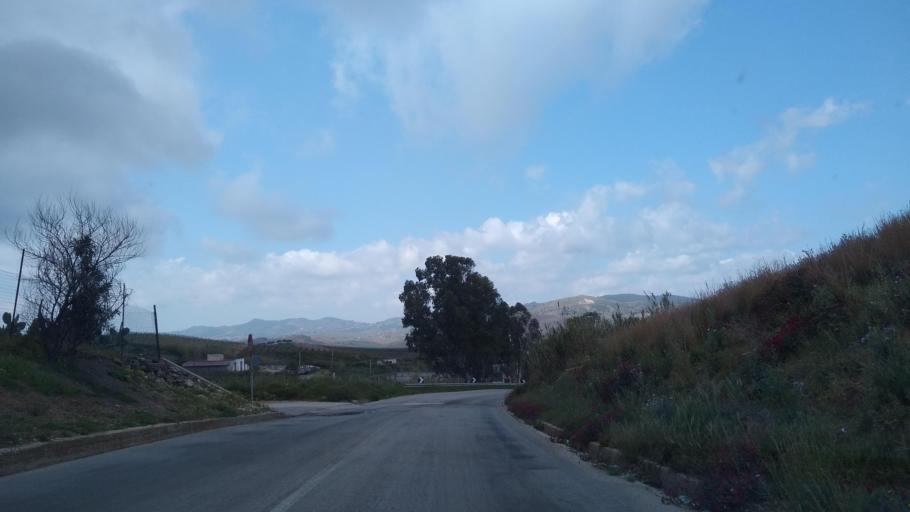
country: IT
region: Sicily
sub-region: Trapani
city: Alcamo
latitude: 37.9715
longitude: 12.9327
